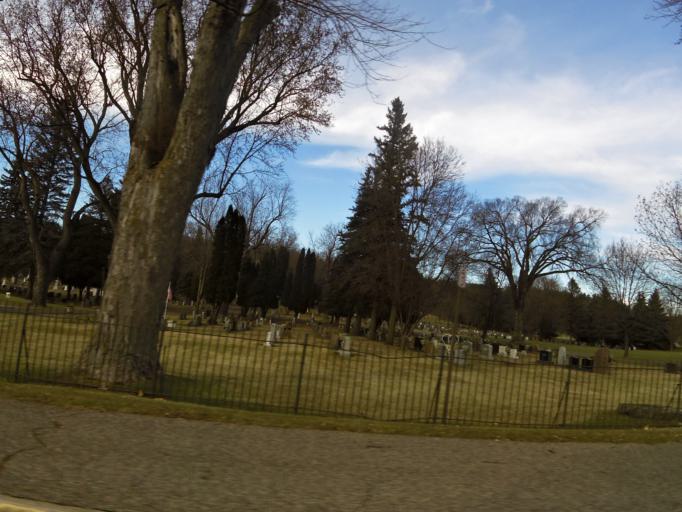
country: US
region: Wisconsin
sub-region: Pierce County
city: River Falls
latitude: 44.8626
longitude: -92.6143
